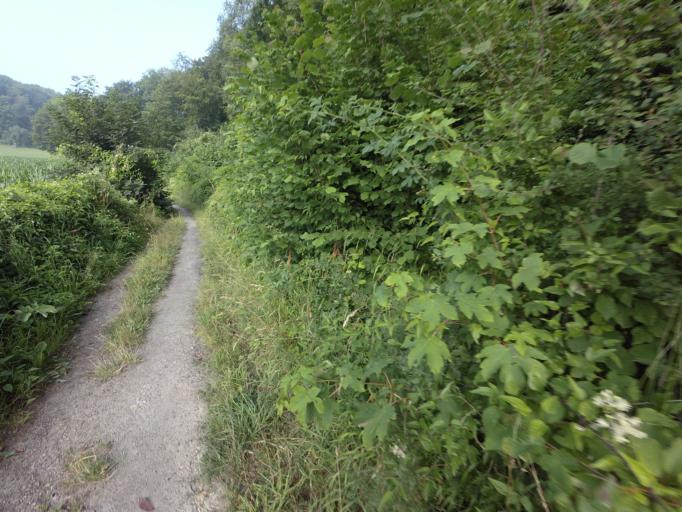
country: BE
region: Wallonia
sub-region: Province de Liege
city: Plombieres
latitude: 50.7620
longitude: 5.8968
